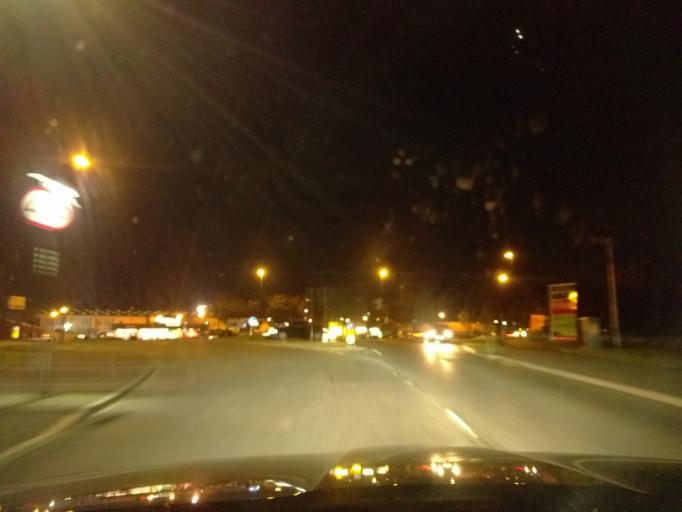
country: GB
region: England
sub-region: Borough of North Tyneside
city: Wallsend
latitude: 55.0144
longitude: -1.5485
